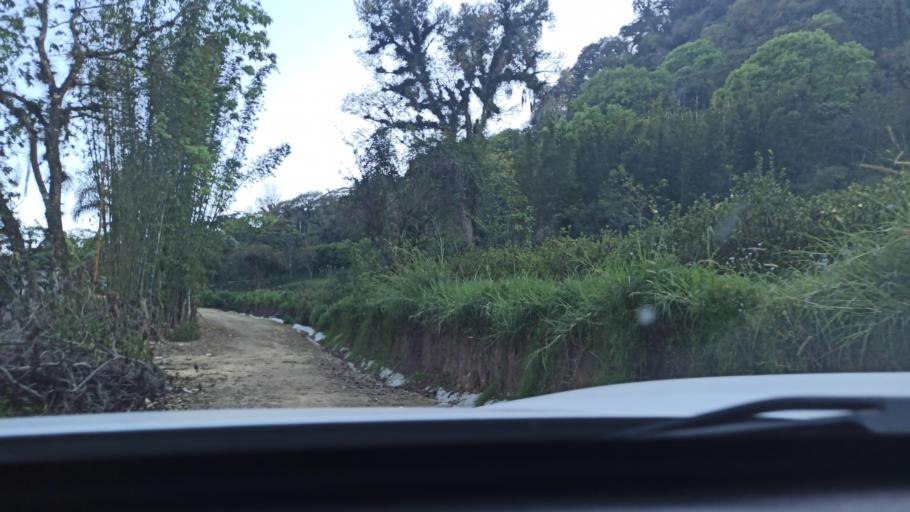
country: MX
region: Veracruz
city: Atzacan
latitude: 18.9072
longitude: -97.0901
